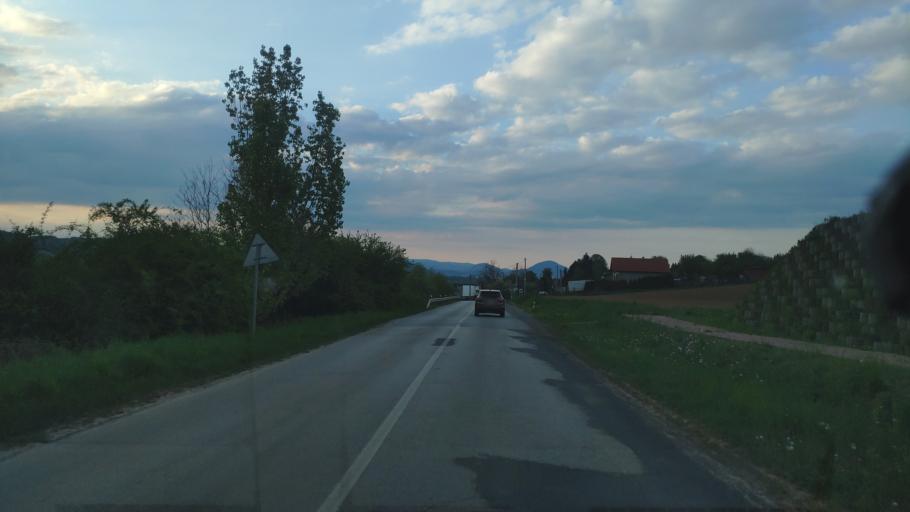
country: SK
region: Presovsky
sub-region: Okres Presov
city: Presov
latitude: 48.9062
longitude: 21.2620
